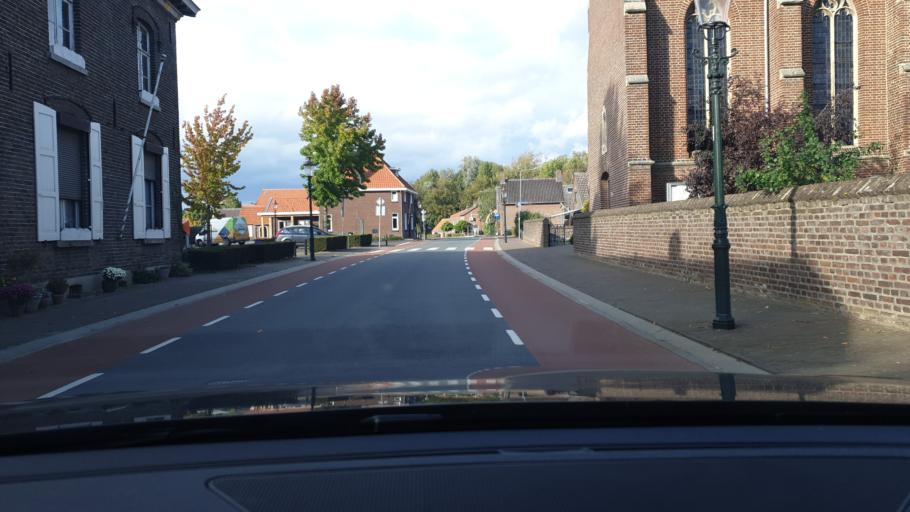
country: NL
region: Limburg
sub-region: Gemeente Venlo
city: Arcen
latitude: 51.4857
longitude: 6.1637
